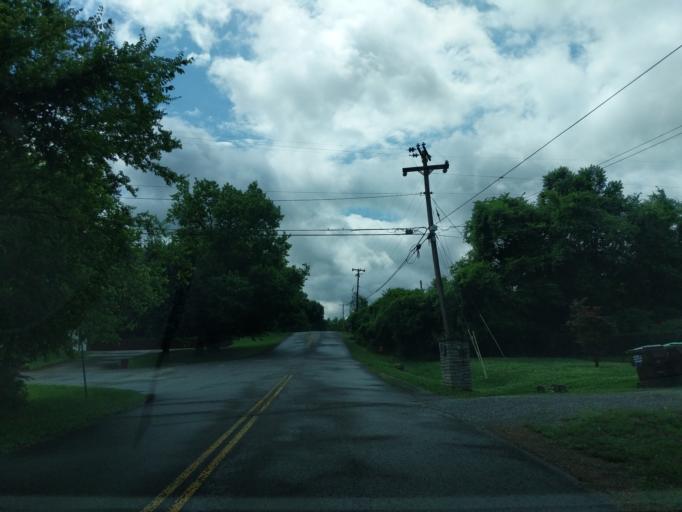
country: US
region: Tennessee
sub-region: Davidson County
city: Lakewood
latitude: 36.2406
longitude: -86.6806
